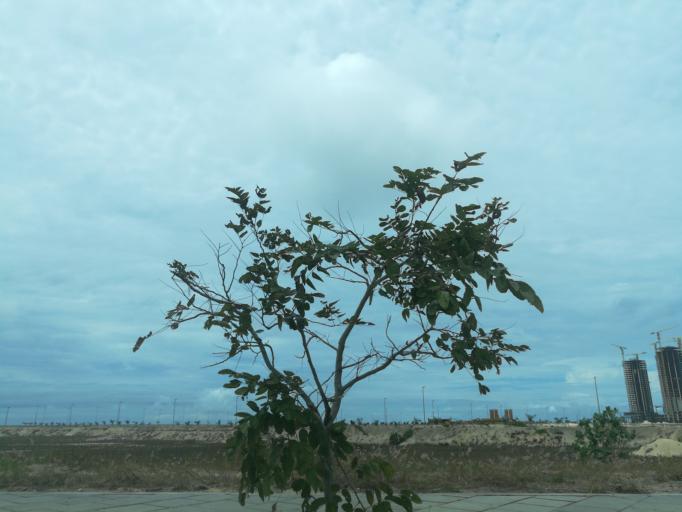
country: NG
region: Lagos
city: Ikoyi
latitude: 6.4080
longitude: 3.4153
